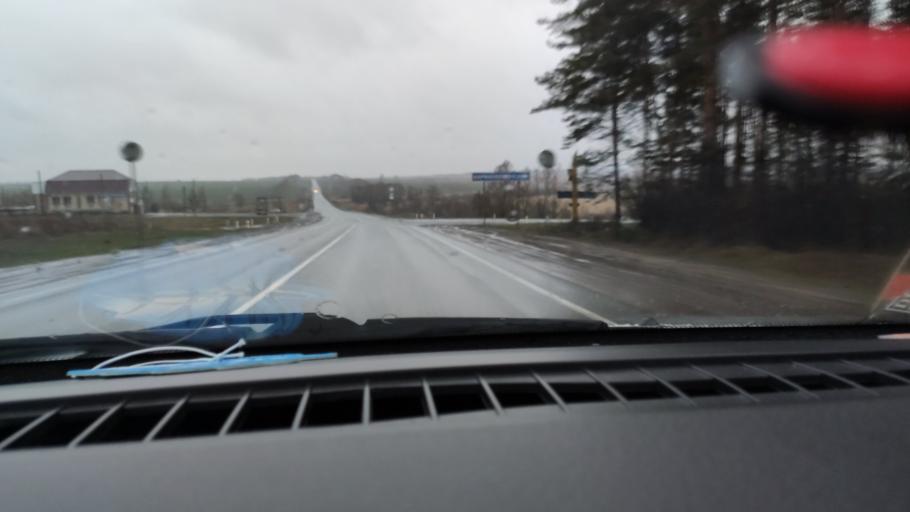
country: RU
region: Tatarstan
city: Mendeleyevsk
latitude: 55.9397
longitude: 52.2899
